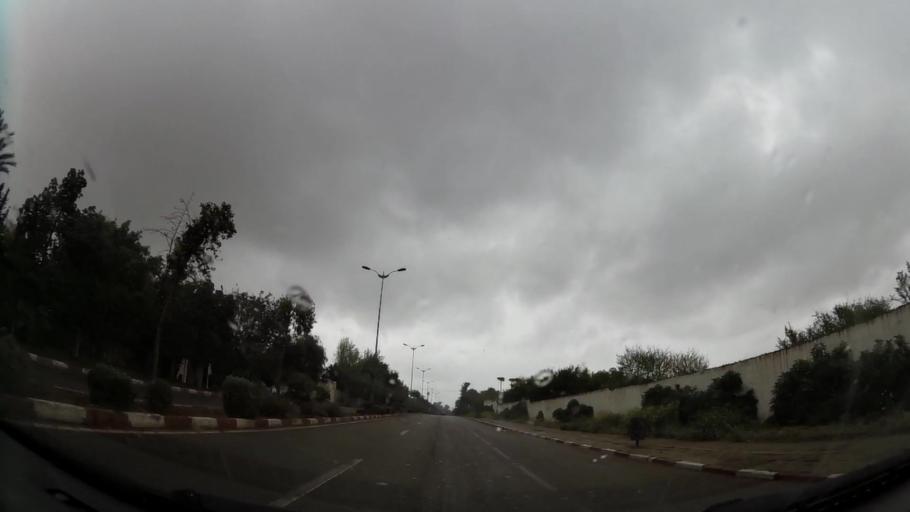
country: MA
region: Grand Casablanca
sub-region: Casablanca
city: Casablanca
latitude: 33.5251
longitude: -7.6313
